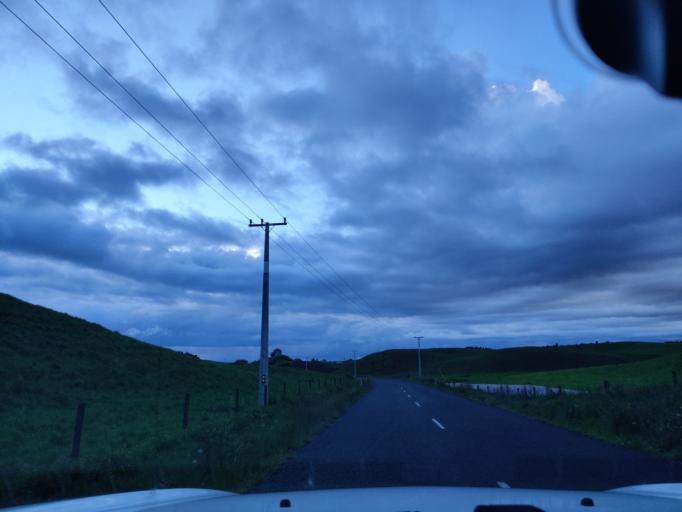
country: NZ
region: Waikato
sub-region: South Waikato District
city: Tokoroa
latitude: -38.1742
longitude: 175.7739
